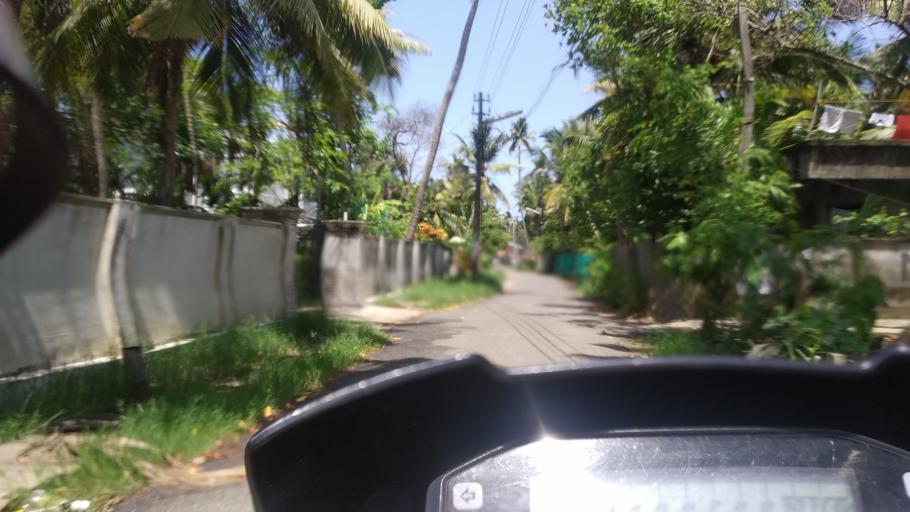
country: IN
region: Kerala
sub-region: Ernakulam
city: Elur
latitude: 10.0733
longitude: 76.2078
